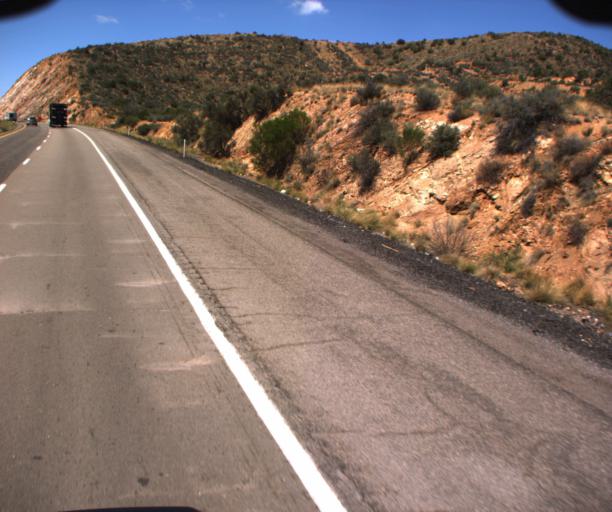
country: US
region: Arizona
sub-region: Mohave County
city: Peach Springs
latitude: 35.1663
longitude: -113.5303
